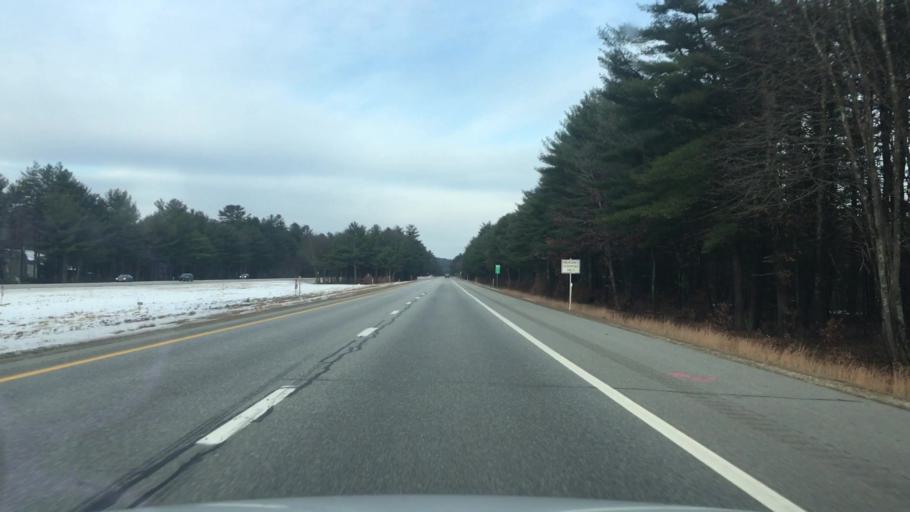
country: US
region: New Hampshire
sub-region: Merrimack County
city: Contoocook
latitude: 43.2225
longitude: -71.7277
